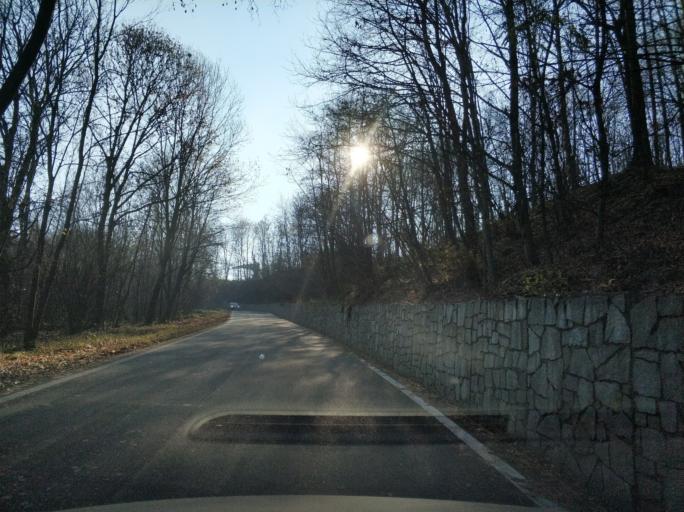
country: IT
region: Piedmont
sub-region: Provincia di Torino
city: Rocca Canavese
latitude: 45.3047
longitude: 7.5775
